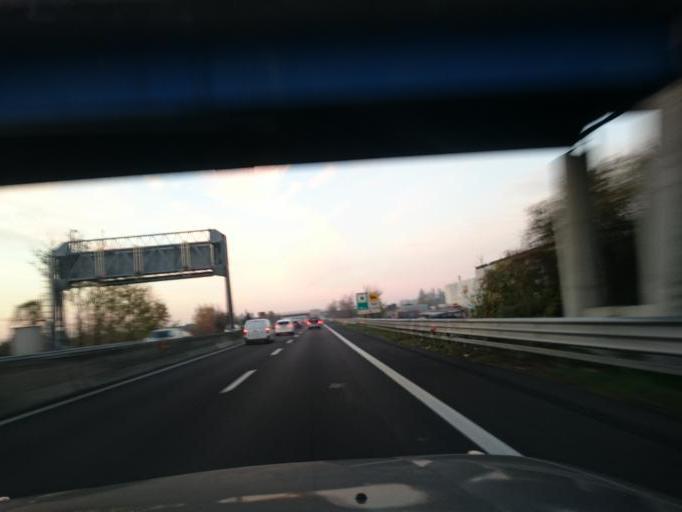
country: IT
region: Veneto
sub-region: Provincia di Padova
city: Terradura
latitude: 45.3260
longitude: 11.8334
